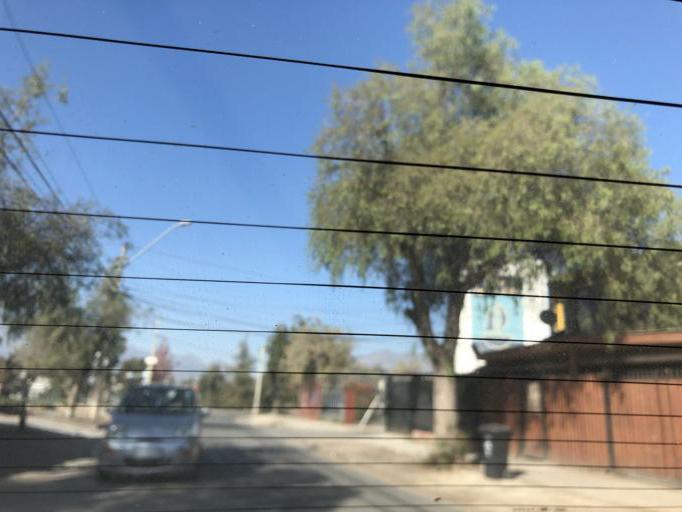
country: CL
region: Santiago Metropolitan
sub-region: Provincia de Cordillera
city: Puente Alto
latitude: -33.6248
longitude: -70.5918
